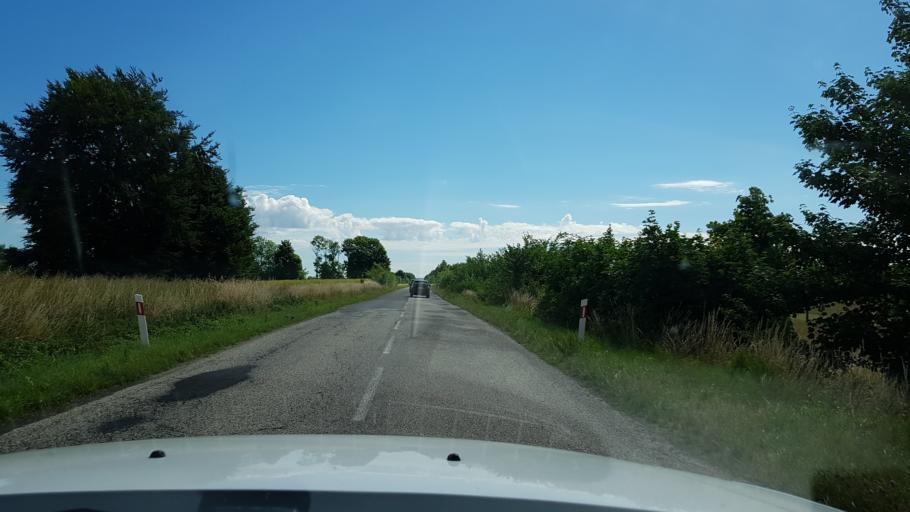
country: PL
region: West Pomeranian Voivodeship
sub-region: Powiat gryficki
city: Trzebiatow
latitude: 54.0374
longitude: 15.1988
